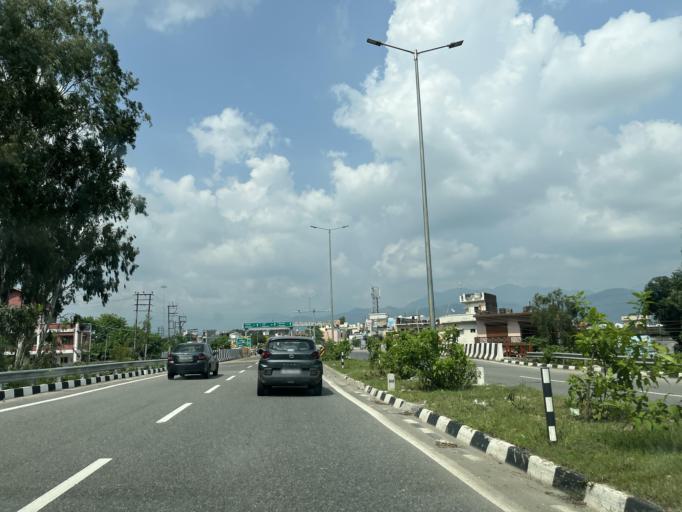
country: IN
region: Uttarakhand
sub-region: Dehradun
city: Raipur
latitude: 30.2519
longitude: 78.0934
